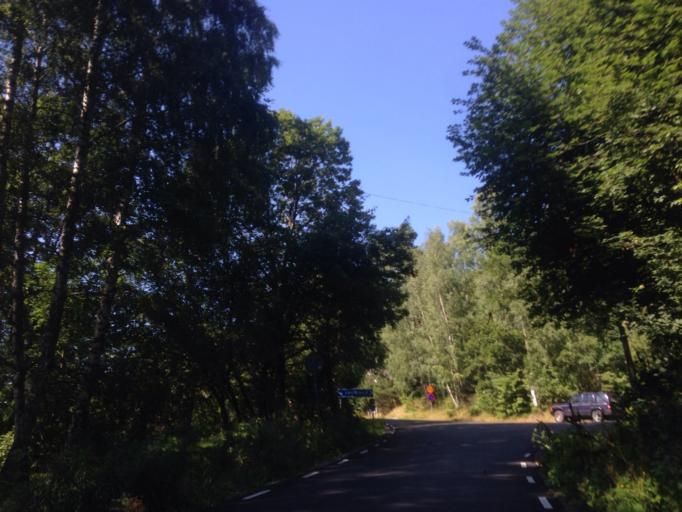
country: SE
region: Stockholm
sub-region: Vaxholms Kommun
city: Vaxholm
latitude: 59.3843
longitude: 18.3604
